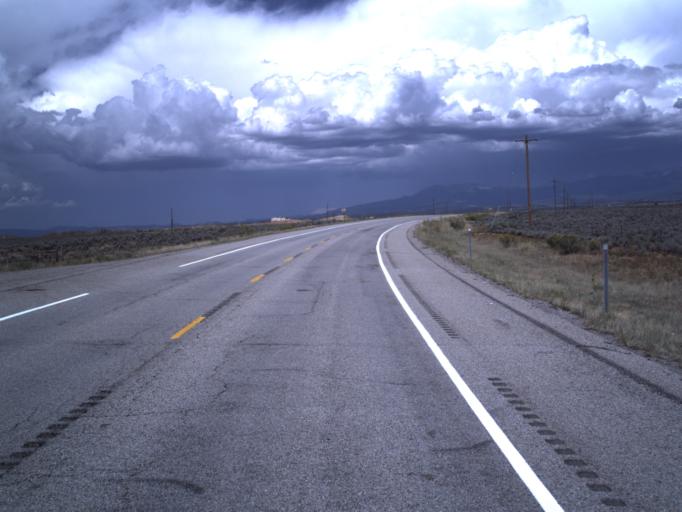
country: US
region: Utah
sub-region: San Juan County
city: Blanding
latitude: 37.5138
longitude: -109.4936
